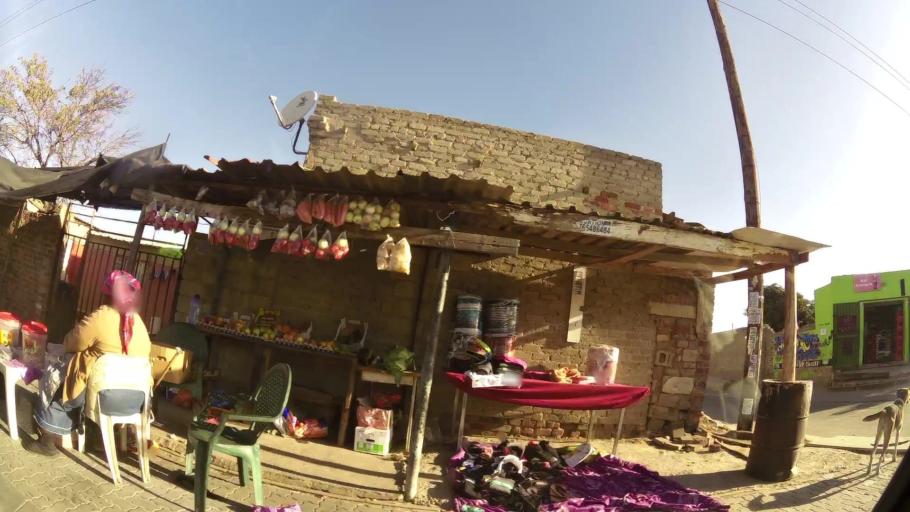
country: ZA
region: Gauteng
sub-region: City of Johannesburg Metropolitan Municipality
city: Diepsloot
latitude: -25.9279
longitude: 28.0042
